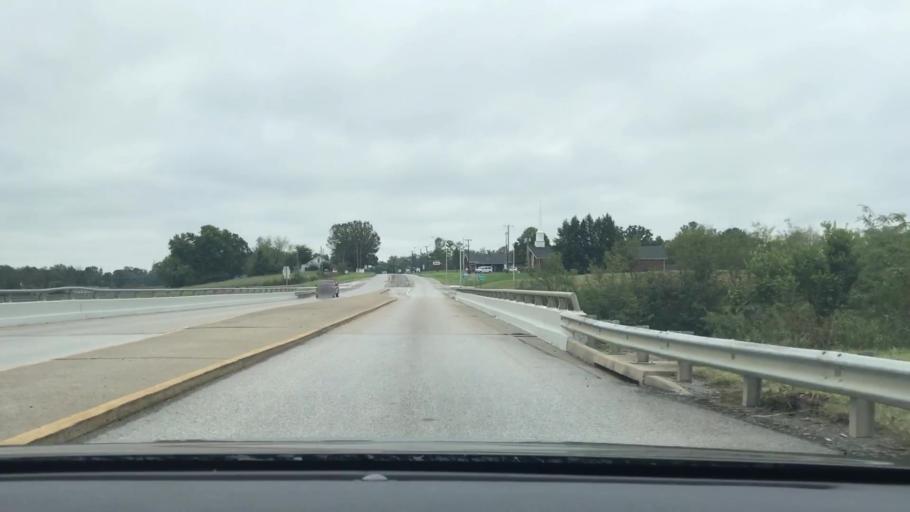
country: US
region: Kentucky
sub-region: Adair County
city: Columbia
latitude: 37.0889
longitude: -85.3034
